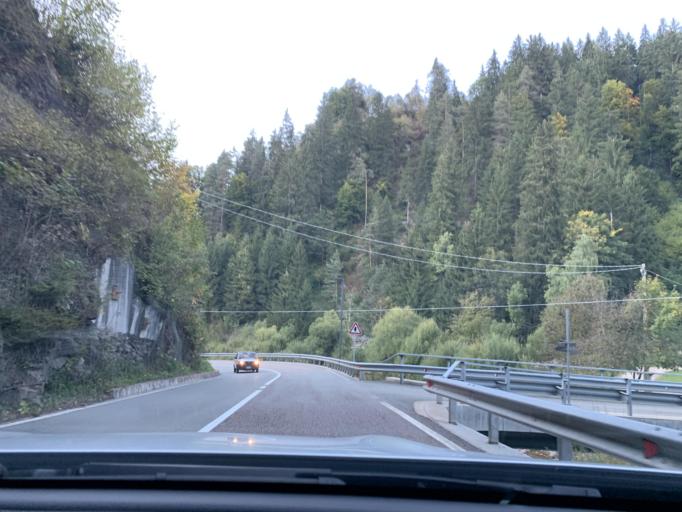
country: IT
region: Trentino-Alto Adige
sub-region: Bolzano
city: Nova Levante
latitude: 46.4250
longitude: 11.4840
